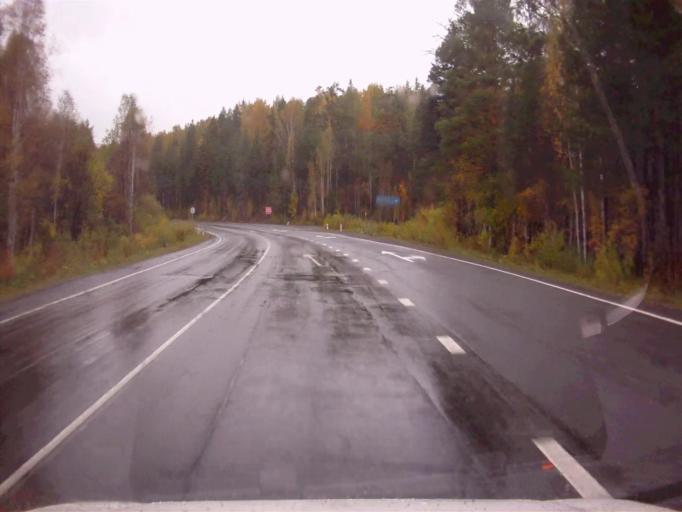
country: RU
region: Chelyabinsk
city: Verkhniy Ufaley
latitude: 55.9655
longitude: 60.3825
